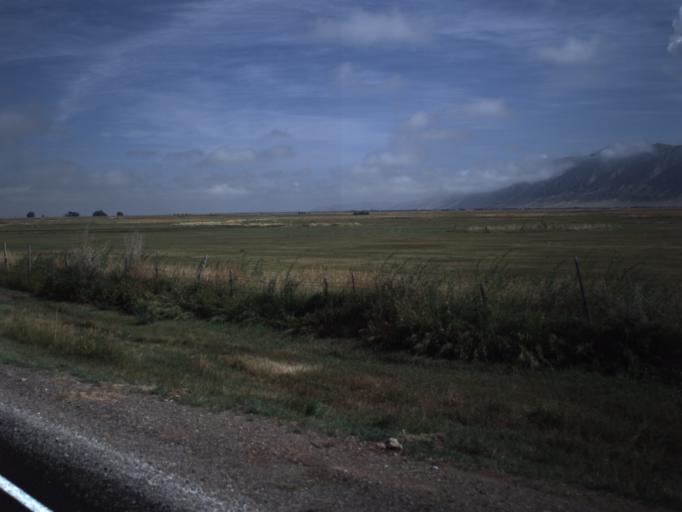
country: US
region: Utah
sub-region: Rich County
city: Randolph
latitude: 41.6164
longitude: -111.1792
